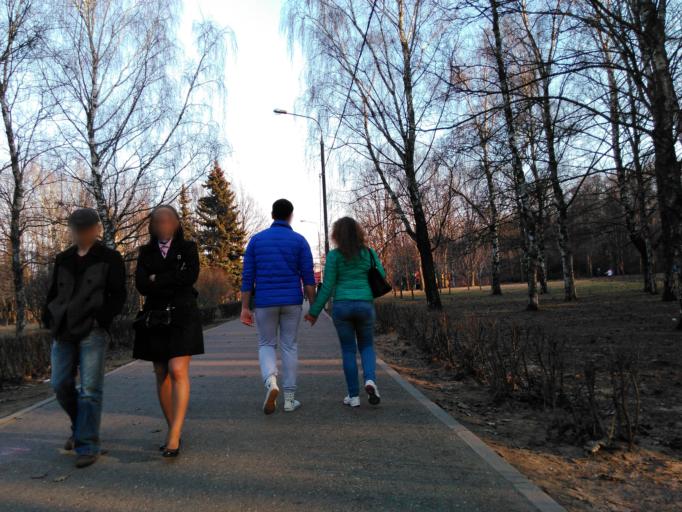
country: RU
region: Moscow
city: Ramenki
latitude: 55.6824
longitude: 37.5025
